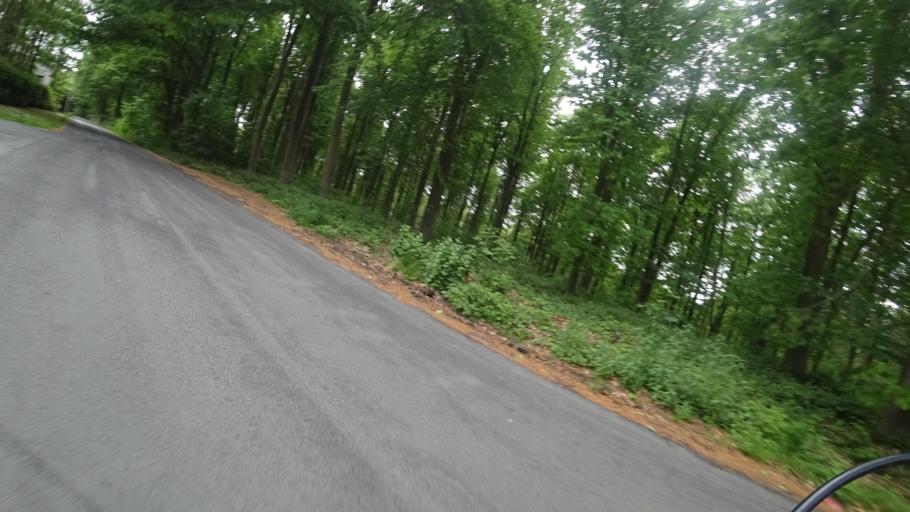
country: BE
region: Wallonia
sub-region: Province du Brabant Wallon
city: Grez-Doiceau
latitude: 50.7337
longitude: 4.6801
